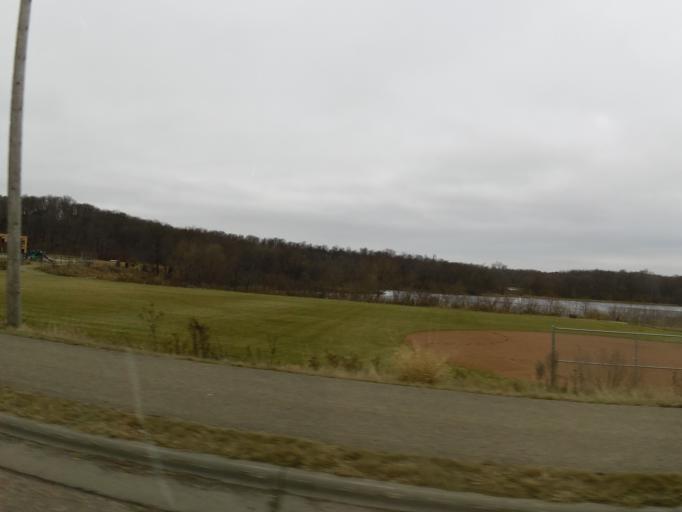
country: US
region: Minnesota
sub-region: Scott County
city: Prior Lake
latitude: 44.7381
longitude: -93.4398
